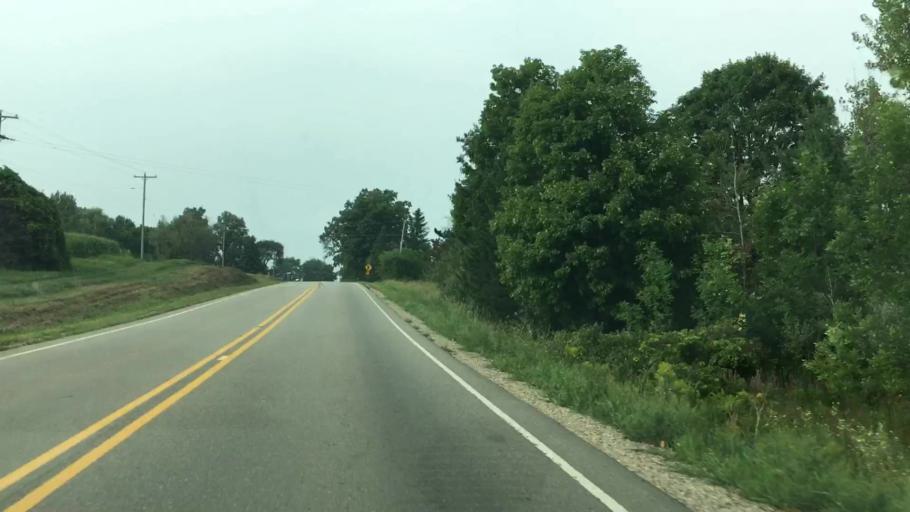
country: US
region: Michigan
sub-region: Ottawa County
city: Hudsonville
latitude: 42.8451
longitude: -85.9006
